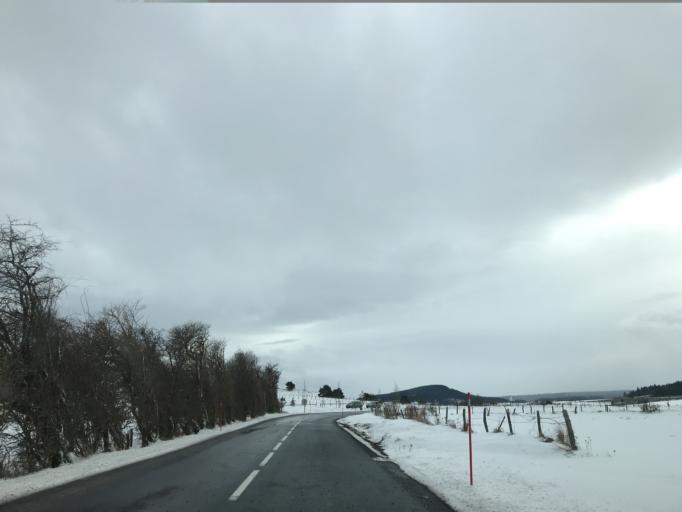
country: FR
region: Auvergne
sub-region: Departement du Puy-de-Dome
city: Aydat
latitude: 45.6702
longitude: 2.9384
